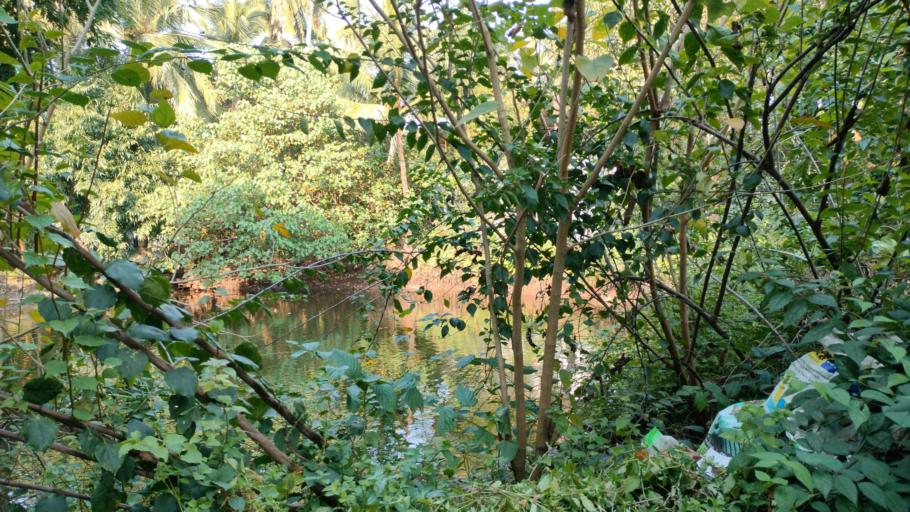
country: IN
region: Maharashtra
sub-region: Thane
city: Bhayandar
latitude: 19.3589
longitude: 72.7891
